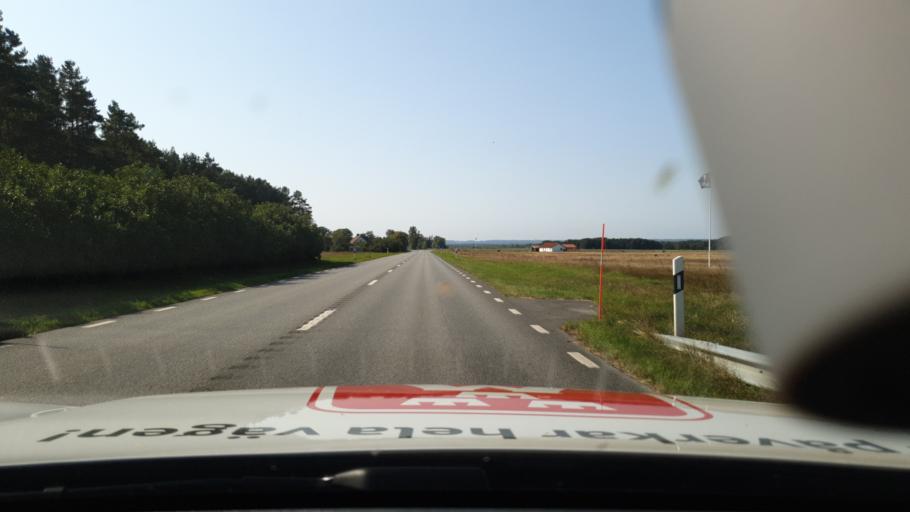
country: SE
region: Skane
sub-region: Kristianstads Kommun
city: Ahus
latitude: 55.8897
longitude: 14.2413
